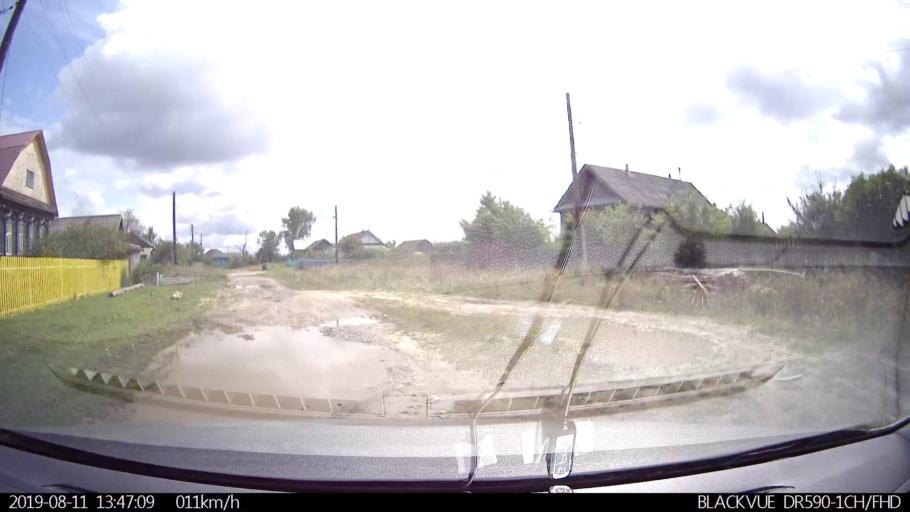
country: RU
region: Ulyanovsk
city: Ignatovka
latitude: 53.8493
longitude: 47.5769
